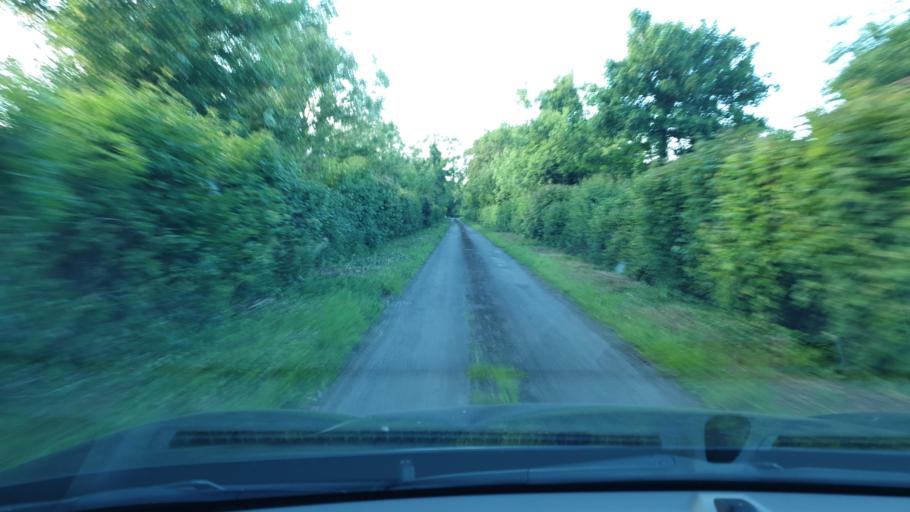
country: IE
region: Leinster
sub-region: An Mhi
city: Ashbourne
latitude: 53.4579
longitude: -6.4079
